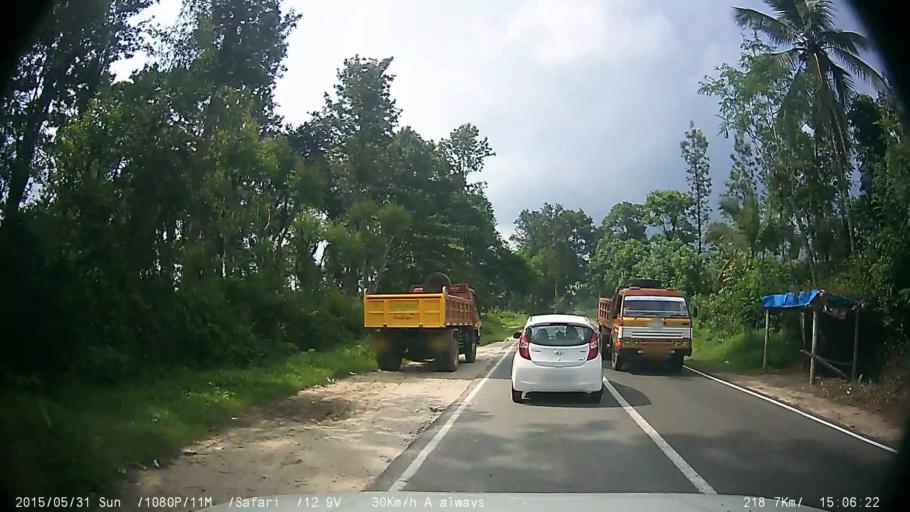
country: IN
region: Kerala
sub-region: Wayanad
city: Kalpetta
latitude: 11.6416
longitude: 76.2136
